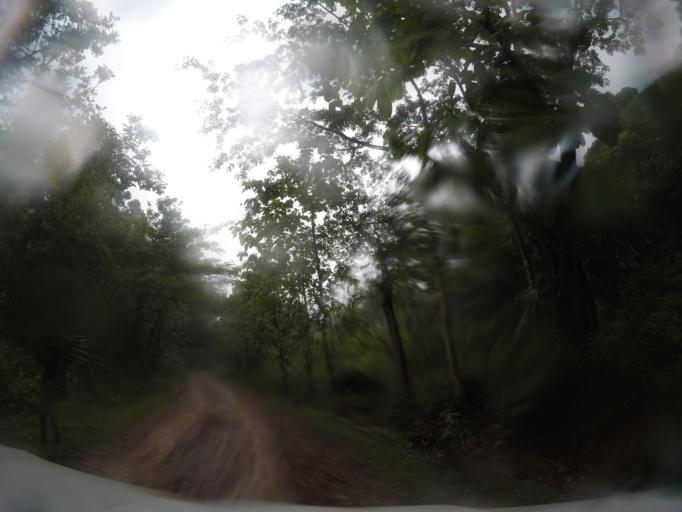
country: TL
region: Baucau
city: Venilale
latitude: -8.6290
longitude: 126.4378
